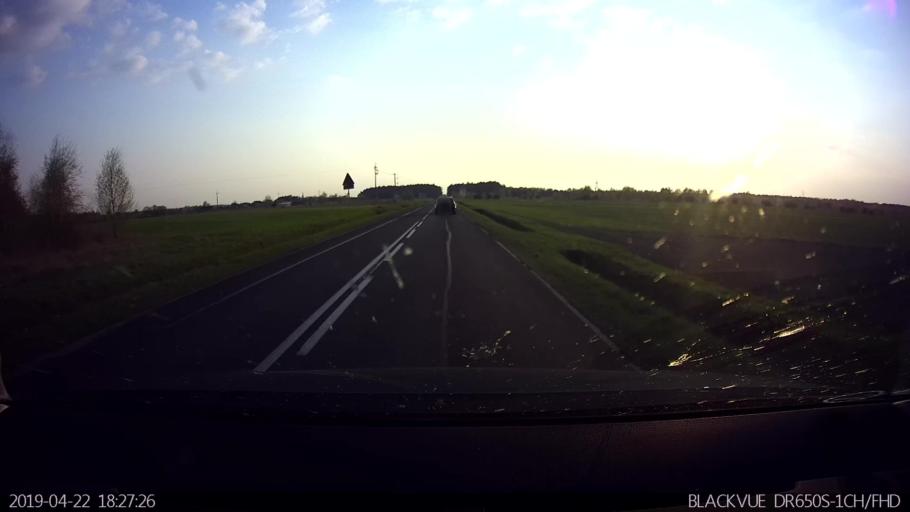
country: PL
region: Masovian Voivodeship
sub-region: Powiat wolominski
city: Tluszcz
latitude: 52.4648
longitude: 21.4965
